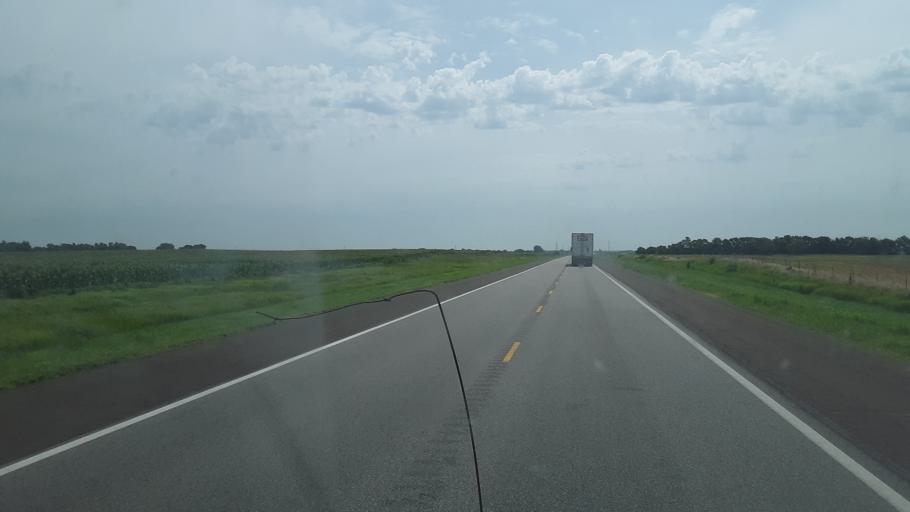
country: US
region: Kansas
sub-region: Reno County
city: South Hutchinson
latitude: 37.9851
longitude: -98.0945
